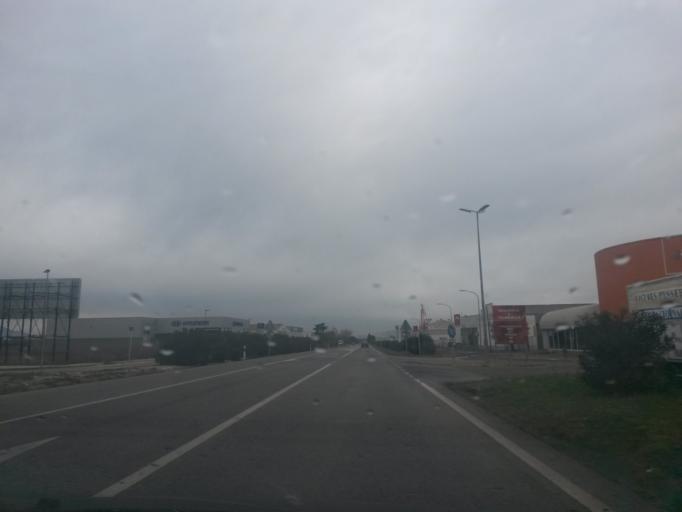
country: ES
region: Catalonia
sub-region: Provincia de Girona
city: Vilamalla
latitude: 42.2302
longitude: 2.9578
